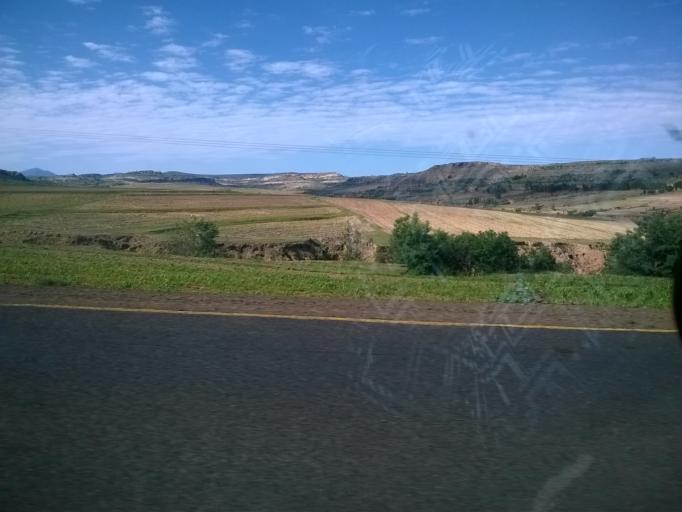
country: LS
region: Berea
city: Teyateyaneng
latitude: -29.0918
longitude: 27.9339
